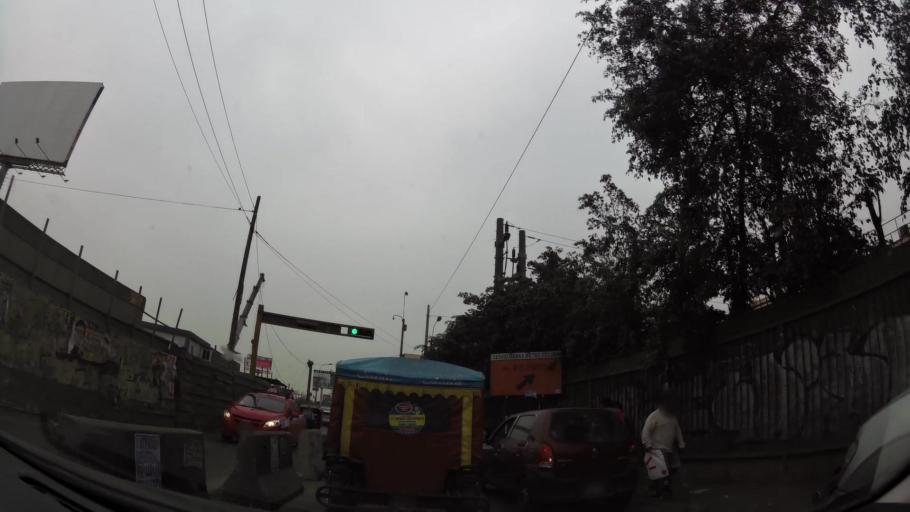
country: PE
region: Lima
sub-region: Lima
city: San Luis
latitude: -12.0564
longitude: -76.9689
